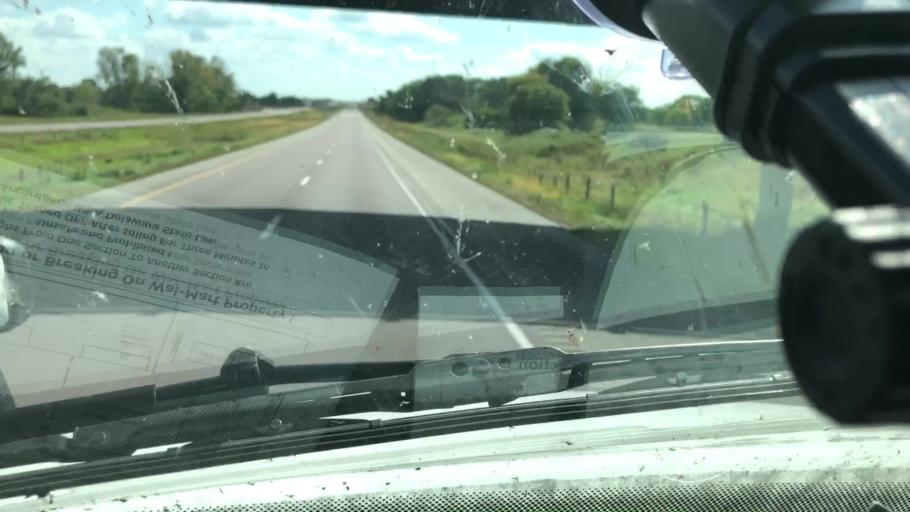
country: US
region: Iowa
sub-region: Worth County
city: Northwood
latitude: 43.3933
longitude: -93.3497
